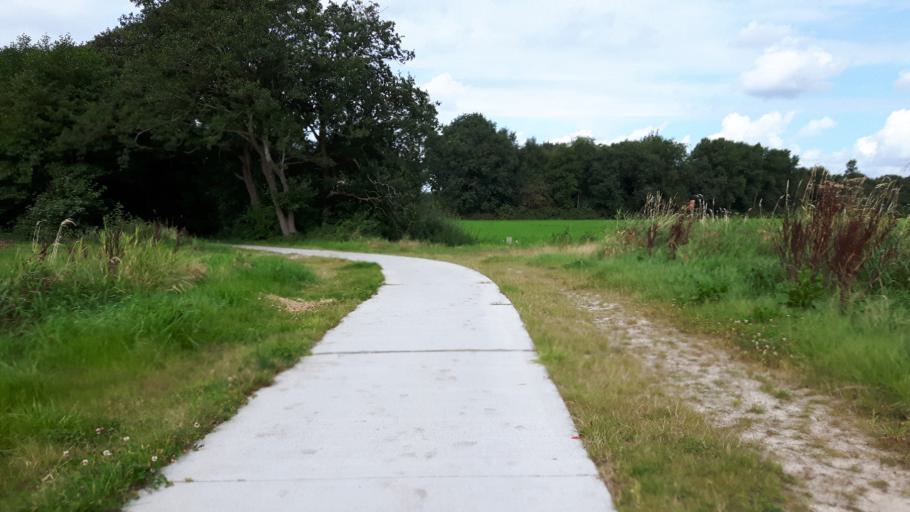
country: NL
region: Groningen
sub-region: Gemeente Leek
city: Leek
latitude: 53.1090
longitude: 6.4396
